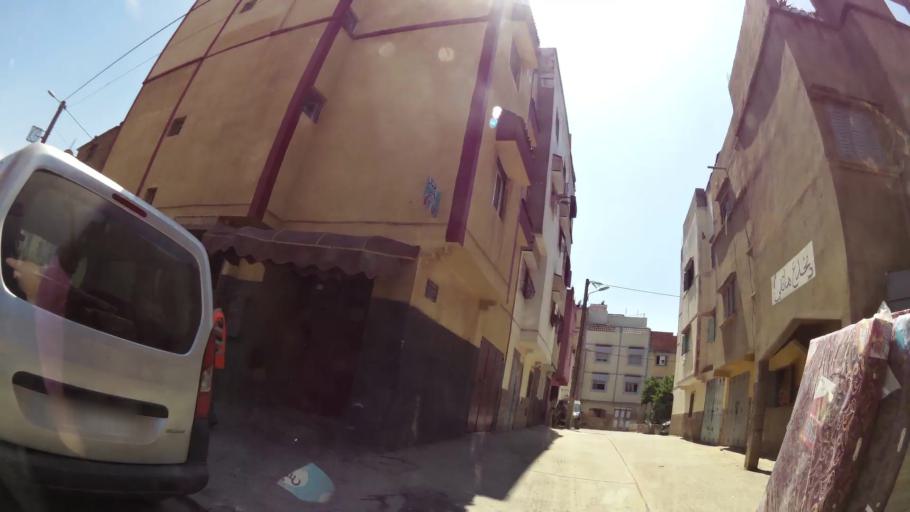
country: MA
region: Rabat-Sale-Zemmour-Zaer
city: Sale
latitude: 34.0599
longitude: -6.7779
